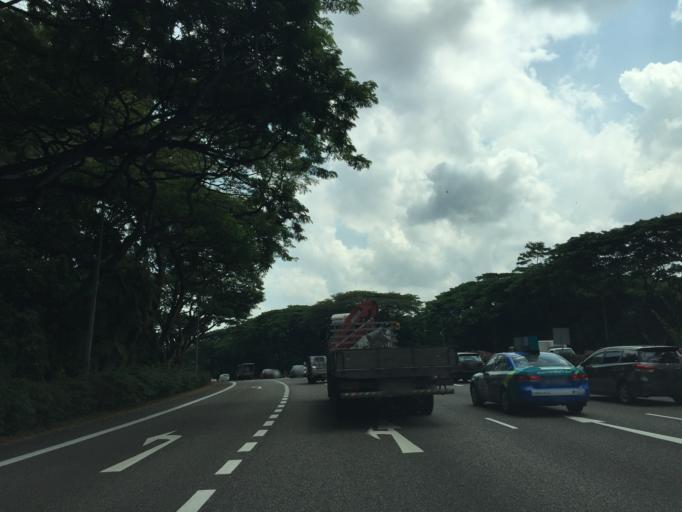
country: SG
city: Singapore
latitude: 1.3264
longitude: 103.8306
